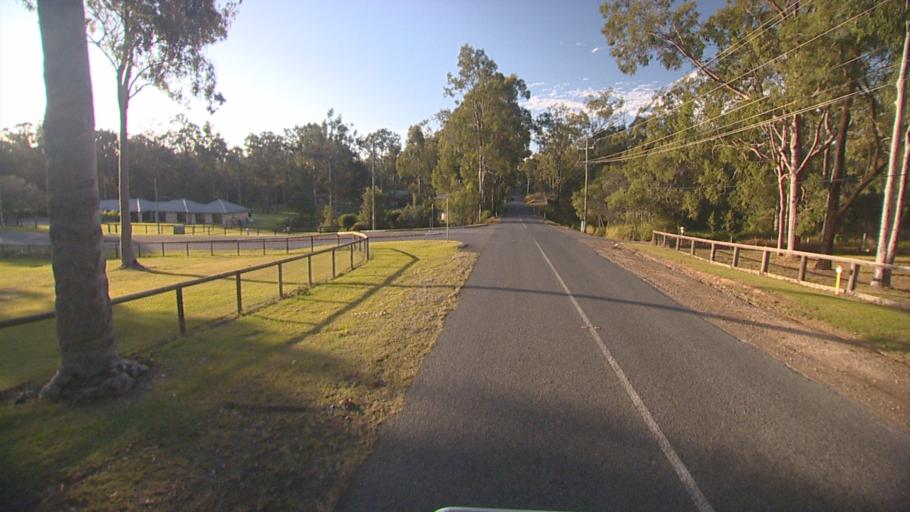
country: AU
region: Queensland
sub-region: Logan
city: Waterford West
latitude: -27.7314
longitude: 153.1461
